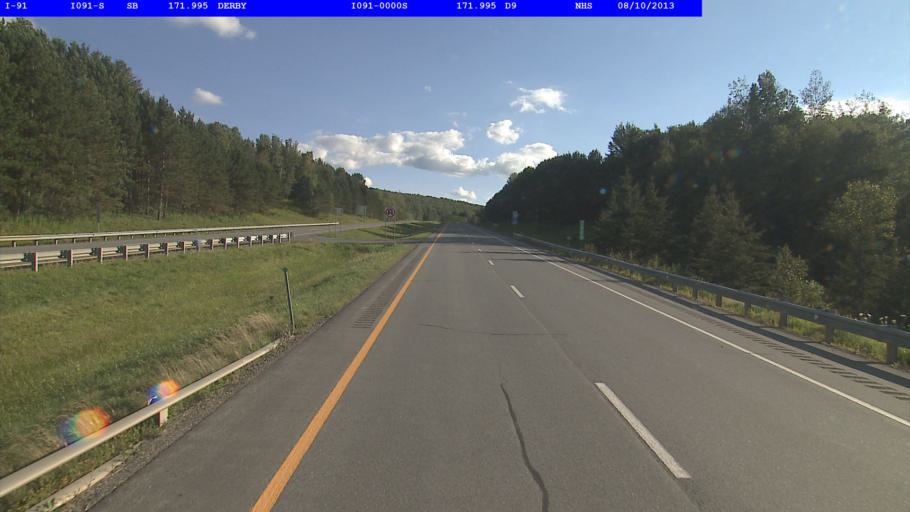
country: US
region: Vermont
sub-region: Orleans County
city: Newport
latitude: 44.9472
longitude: -72.1548
